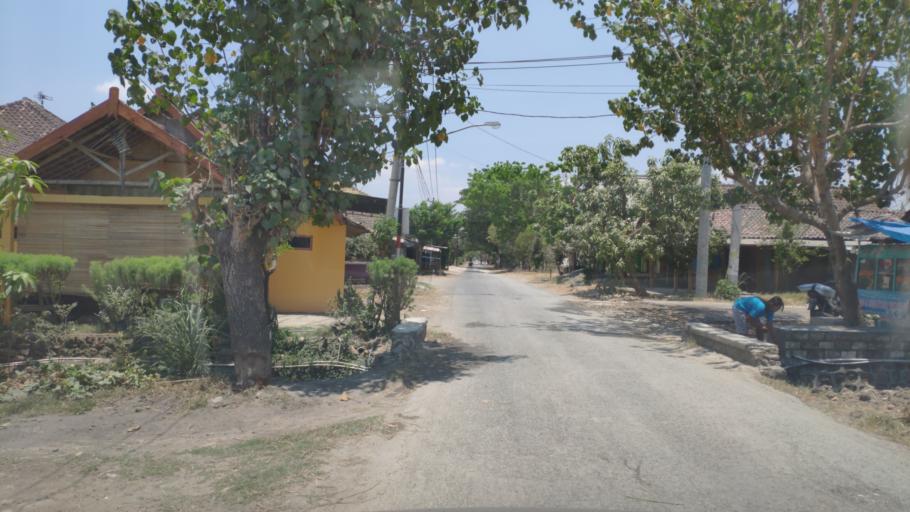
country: ID
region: Central Java
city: Kapuan
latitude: -7.1780
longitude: 111.5599
